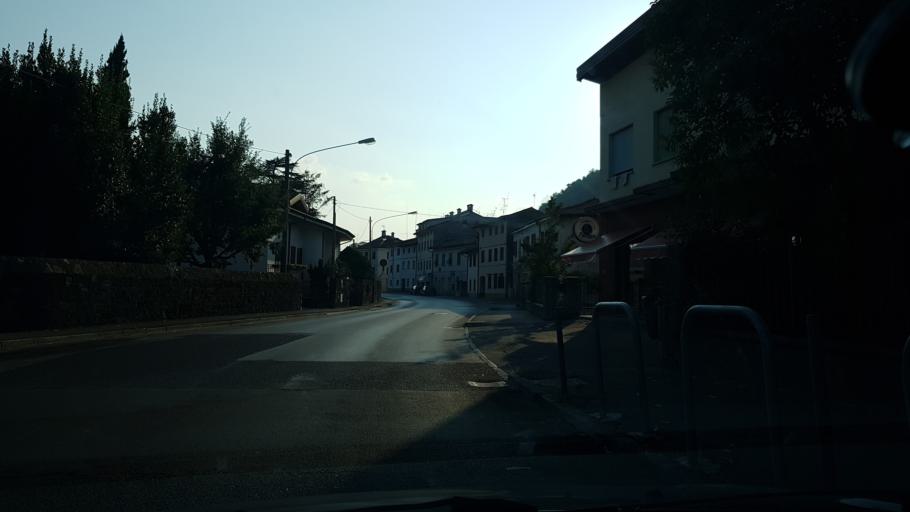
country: IT
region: Friuli Venezia Giulia
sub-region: Provincia di Gorizia
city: Gorizia
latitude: 45.9423
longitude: 13.5984
